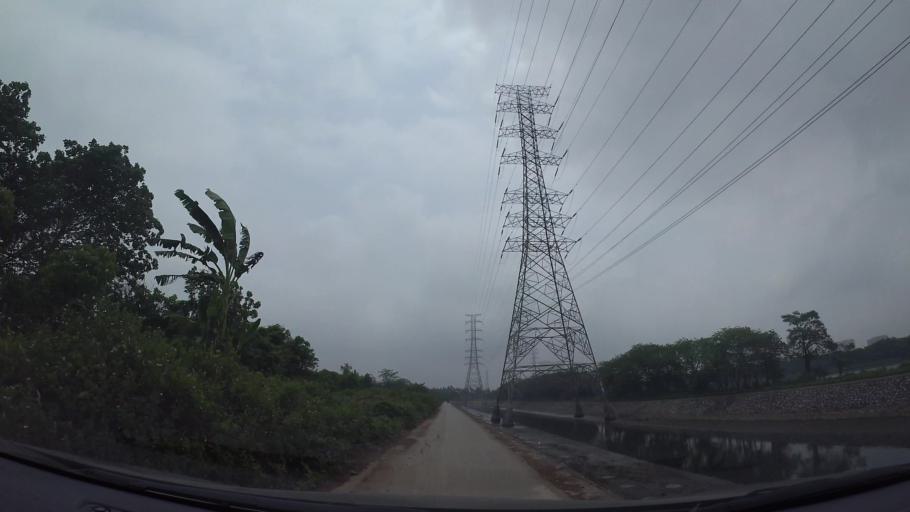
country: VN
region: Ha Noi
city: Van Dien
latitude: 20.9748
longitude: 105.8563
